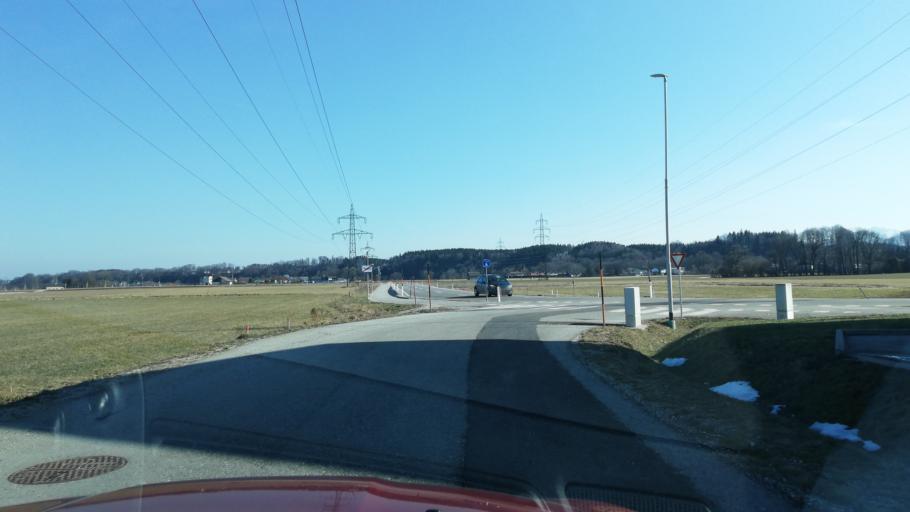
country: AT
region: Upper Austria
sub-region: Politischer Bezirk Vocklabruck
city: Attnang-Puchheim
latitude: 47.9881
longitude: 13.6953
